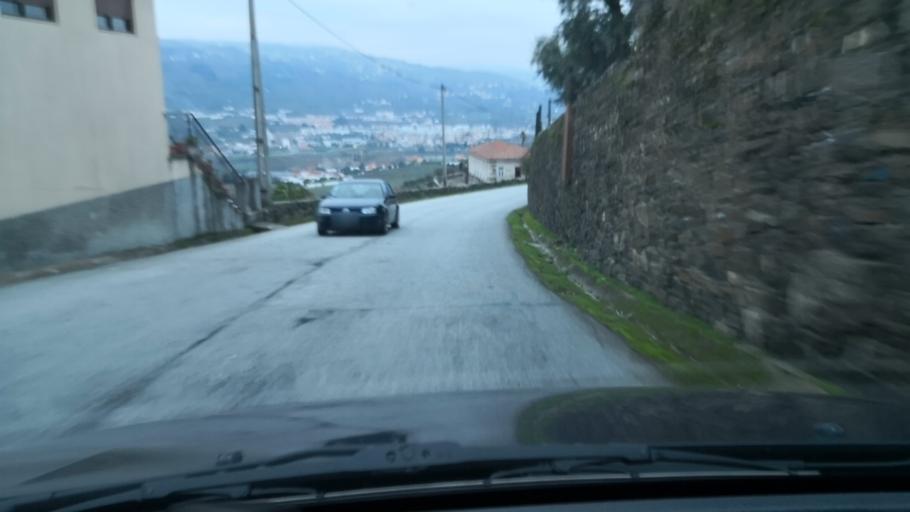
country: PT
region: Vila Real
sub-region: Peso da Regua
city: Peso da Regua
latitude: 41.1445
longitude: -7.7921
